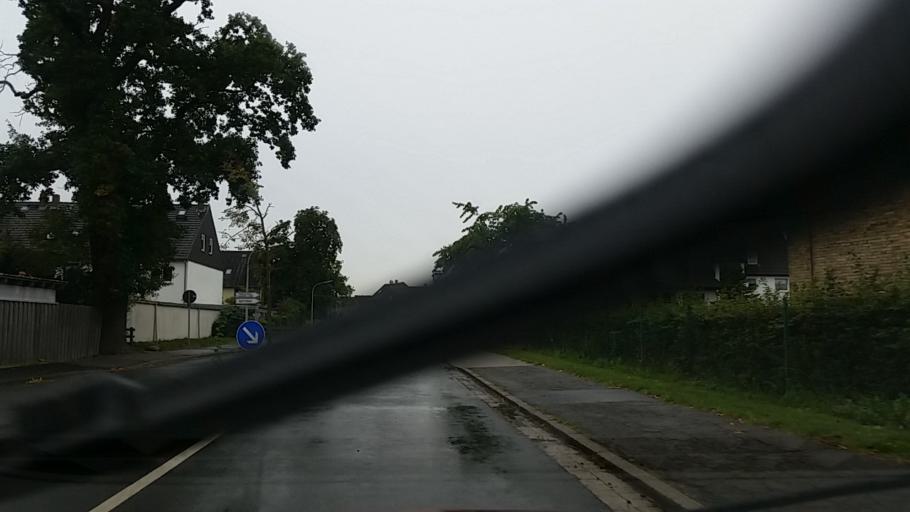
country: DE
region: Lower Saxony
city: Leiferde
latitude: 52.2036
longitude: 10.5080
